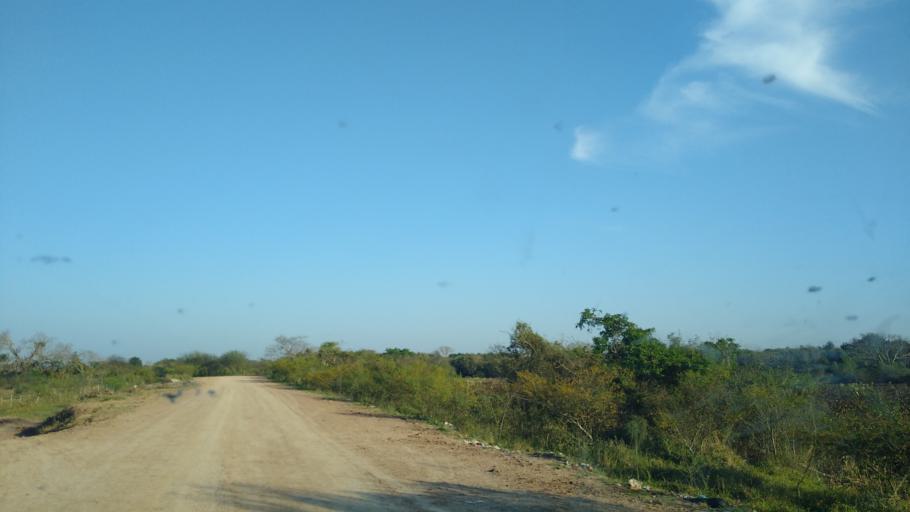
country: AR
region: Chaco
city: Barranqueras
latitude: -27.4645
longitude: -58.9196
